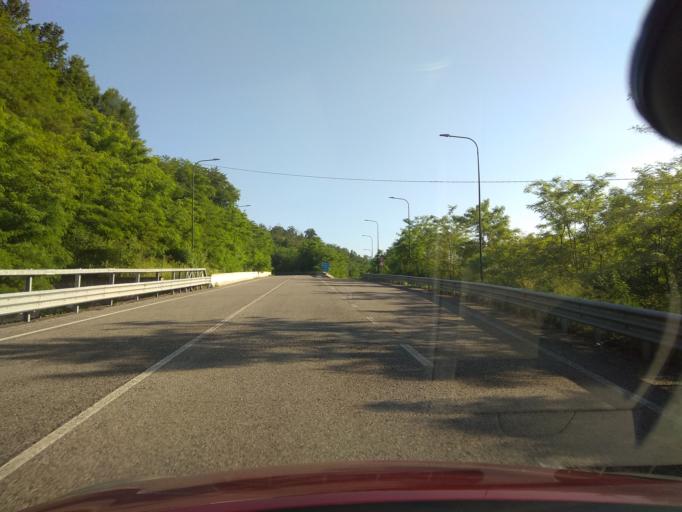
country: IT
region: Piedmont
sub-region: Provincia di Biella
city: Quaregna
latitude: 45.5839
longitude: 8.1725
